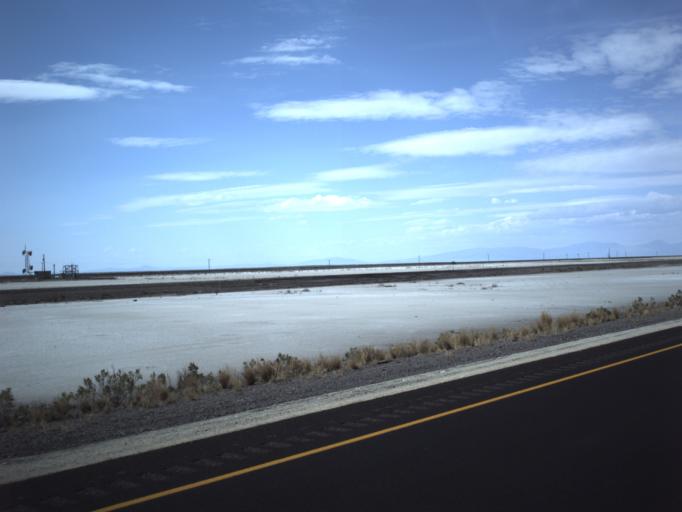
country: US
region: Utah
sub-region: Tooele County
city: Wendover
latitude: 40.7314
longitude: -113.4832
